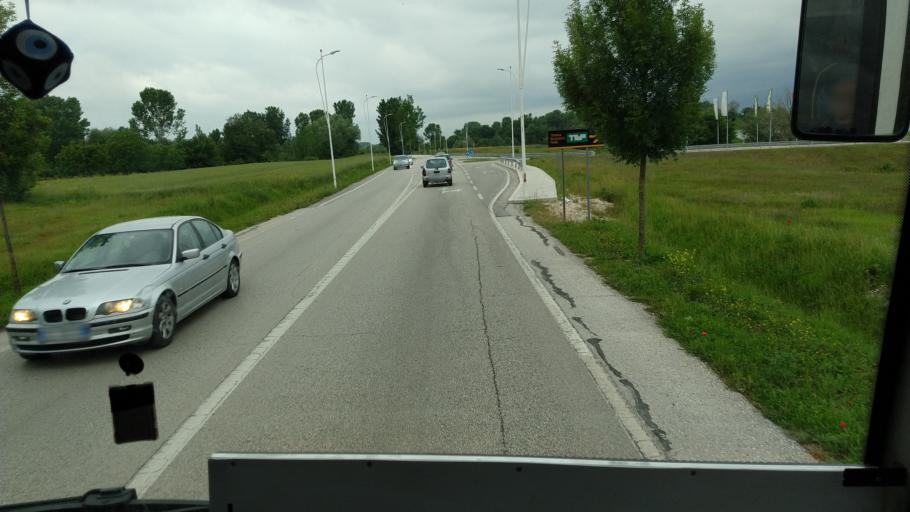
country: AL
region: Tirane
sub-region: Rrethi i Tiranes
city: Berxull
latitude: 41.4084
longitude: 19.7037
